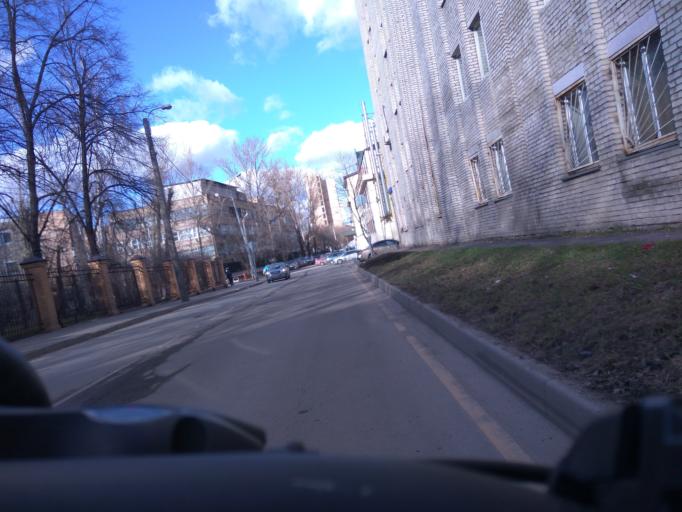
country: RU
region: Moscow
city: Sokol'niki
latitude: 55.8033
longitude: 37.6503
